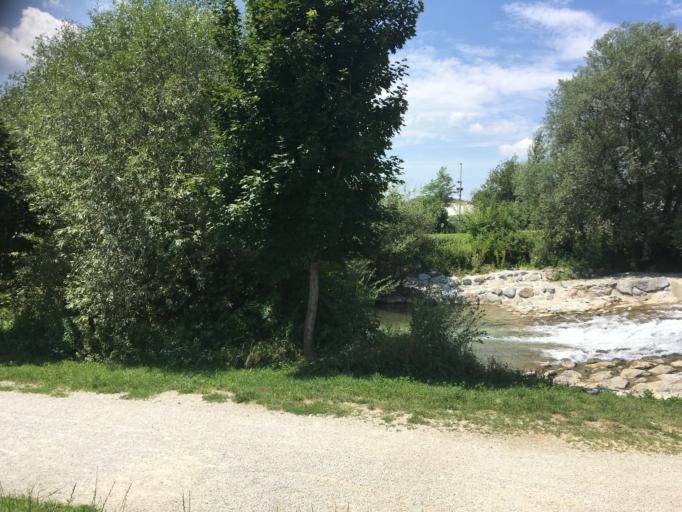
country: SI
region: Menges
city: Preserje pri Radomljah
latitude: 46.1618
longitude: 14.6015
